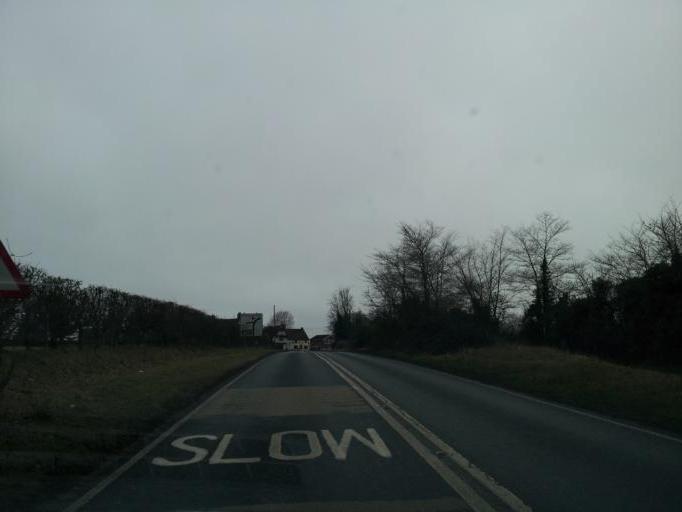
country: GB
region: England
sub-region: Essex
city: Mistley
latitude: 51.9700
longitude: 1.0896
